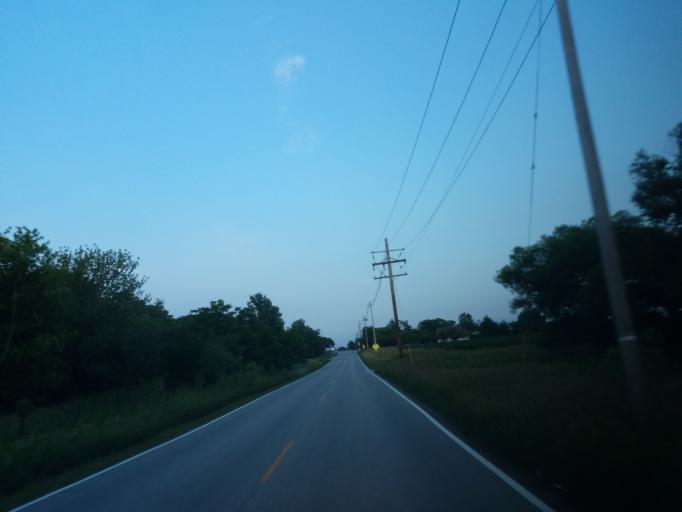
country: US
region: Illinois
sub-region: McLean County
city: Bloomington
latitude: 40.4416
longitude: -88.9975
